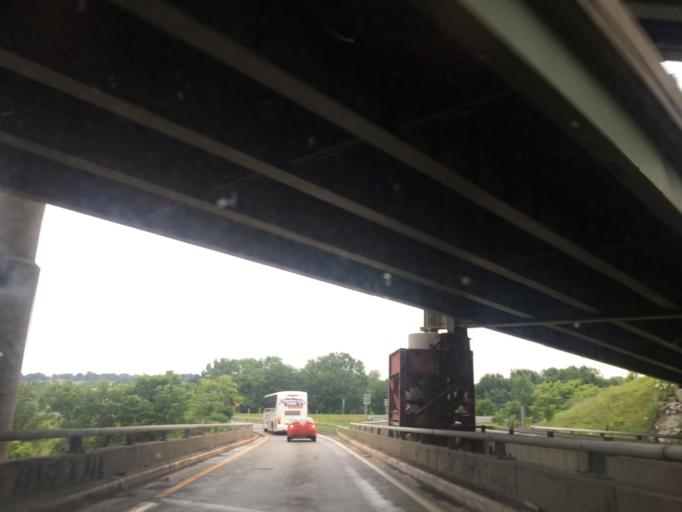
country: US
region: New York
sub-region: Albany County
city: Menands
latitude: 42.6673
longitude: -73.7330
